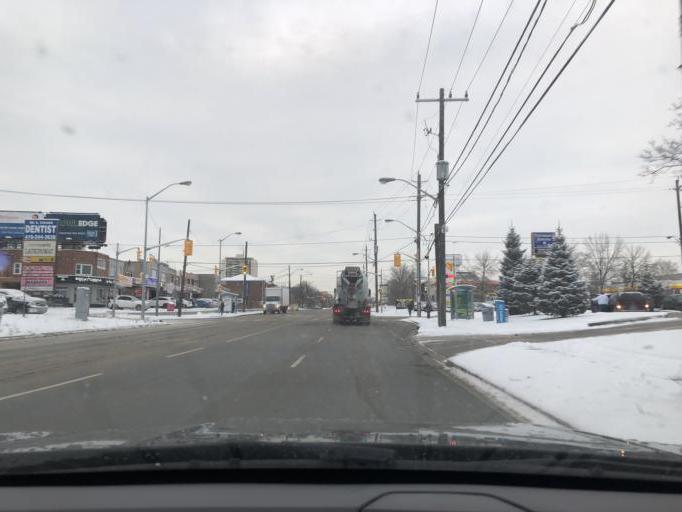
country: CA
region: Ontario
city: Toronto
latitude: 43.7023
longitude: -79.4766
